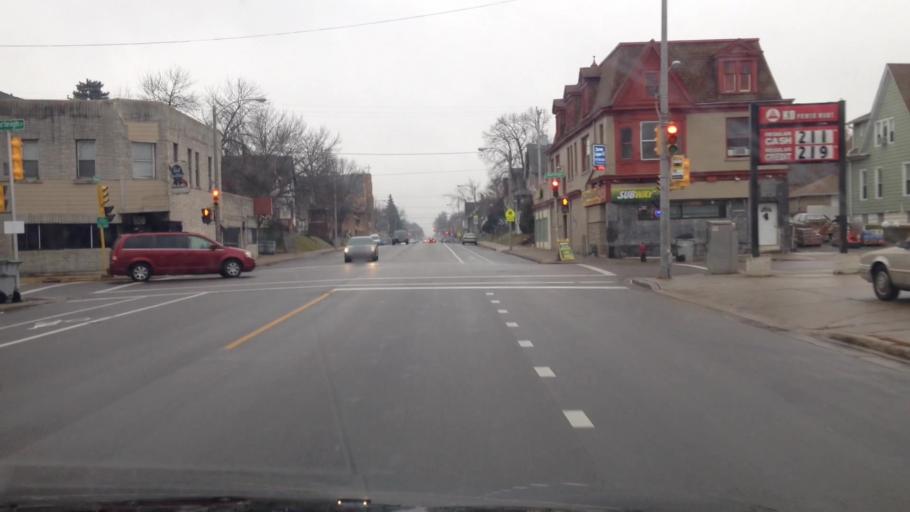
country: US
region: Wisconsin
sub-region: Milwaukee County
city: Shorewood
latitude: 43.0751
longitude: -87.9053
